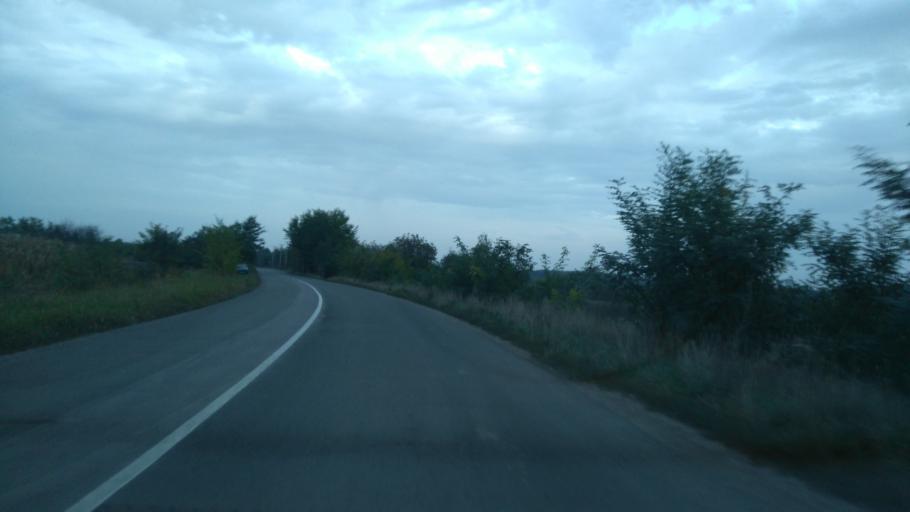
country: RS
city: Mol
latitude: 45.7757
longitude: 20.1340
